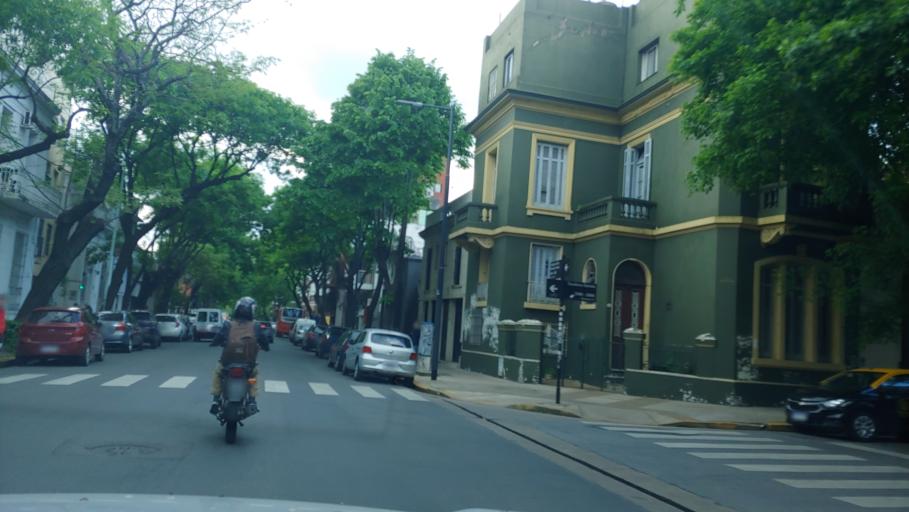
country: AR
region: Buenos Aires F.D.
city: Colegiales
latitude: -34.5765
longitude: -58.4500
